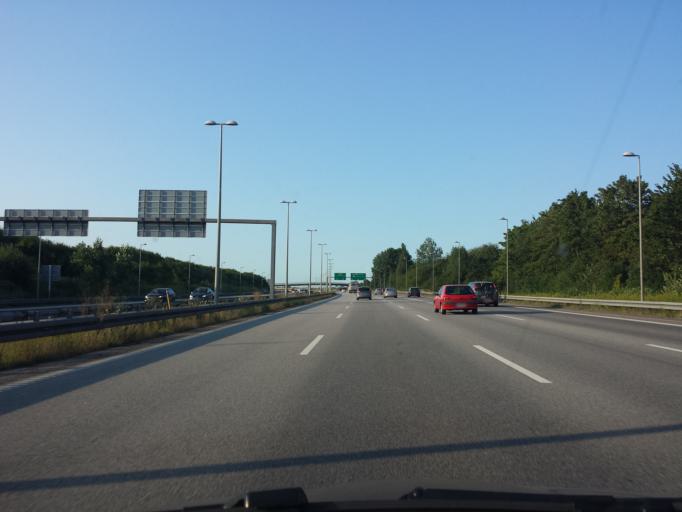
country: DK
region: Capital Region
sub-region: Rodovre Kommune
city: Rodovre
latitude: 55.6801
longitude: 12.4275
